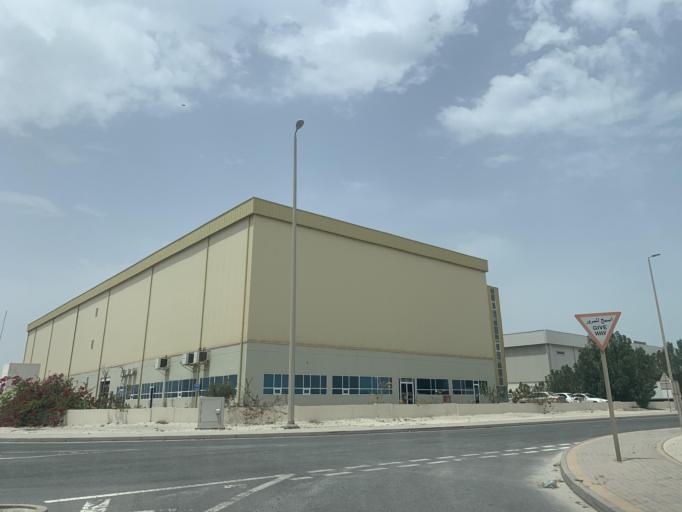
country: BH
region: Muharraq
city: Al Hadd
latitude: 26.2233
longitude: 50.6832
